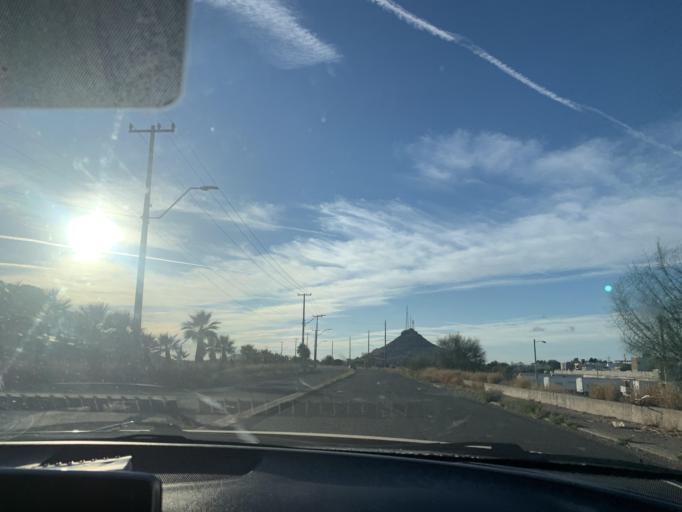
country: MX
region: Sonora
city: Hermosillo
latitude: 29.0737
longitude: -110.9280
